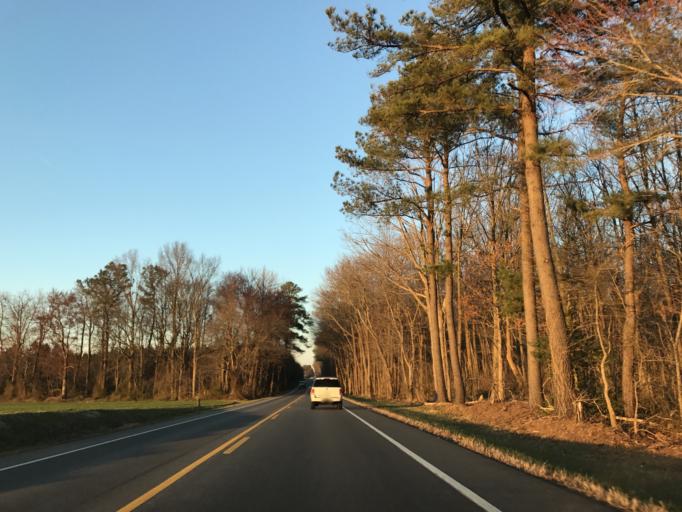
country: US
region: Maryland
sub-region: Talbot County
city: Easton
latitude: 38.8292
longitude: -76.0346
